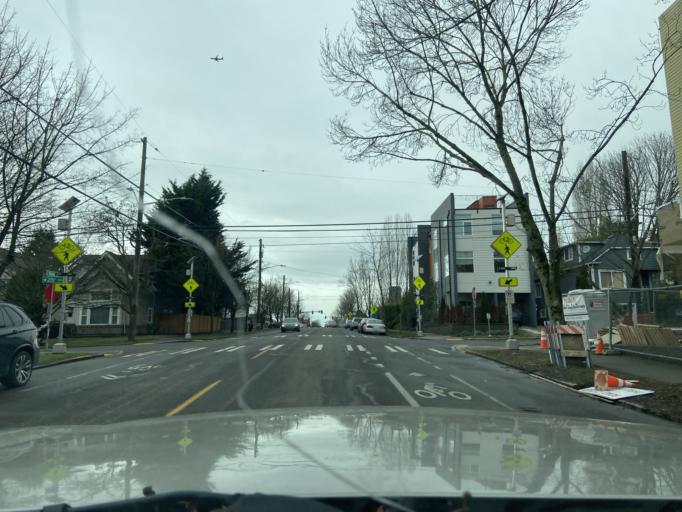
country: US
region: Washington
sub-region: King County
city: Seattle
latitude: 47.6017
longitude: -122.2996
